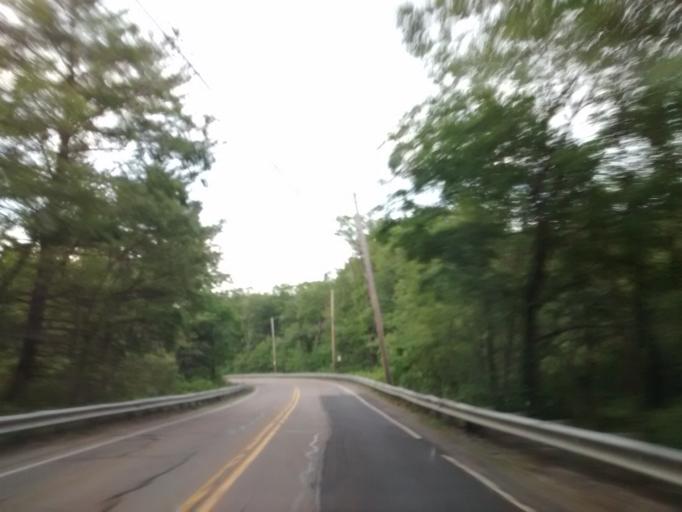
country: US
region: Massachusetts
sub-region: Worcester County
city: Milford
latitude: 42.1803
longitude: -71.5068
